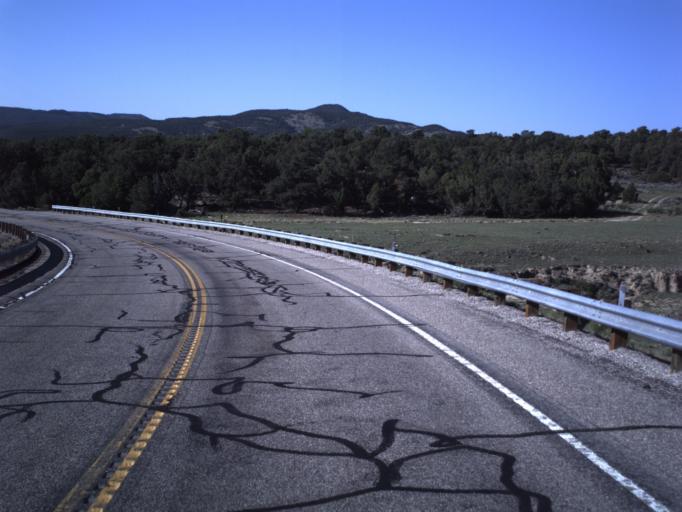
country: US
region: Utah
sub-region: Wayne County
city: Loa
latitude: 38.6895
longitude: -111.4005
